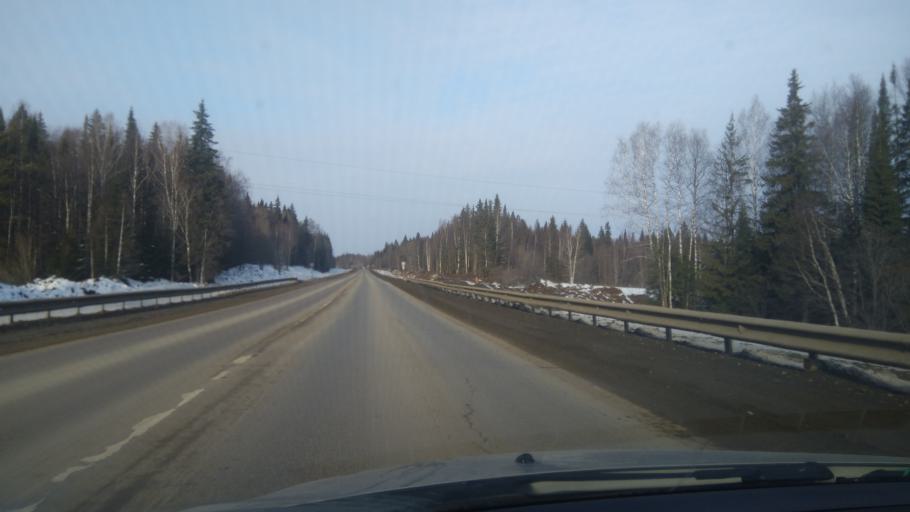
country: RU
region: Sverdlovsk
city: Bisert'
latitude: 56.8281
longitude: 59.1434
